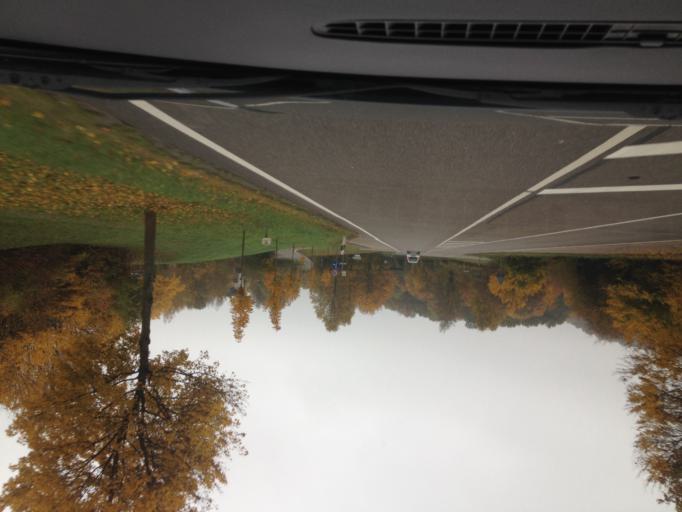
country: DE
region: Saarland
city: Eppelborn
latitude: 49.4561
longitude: 6.9792
